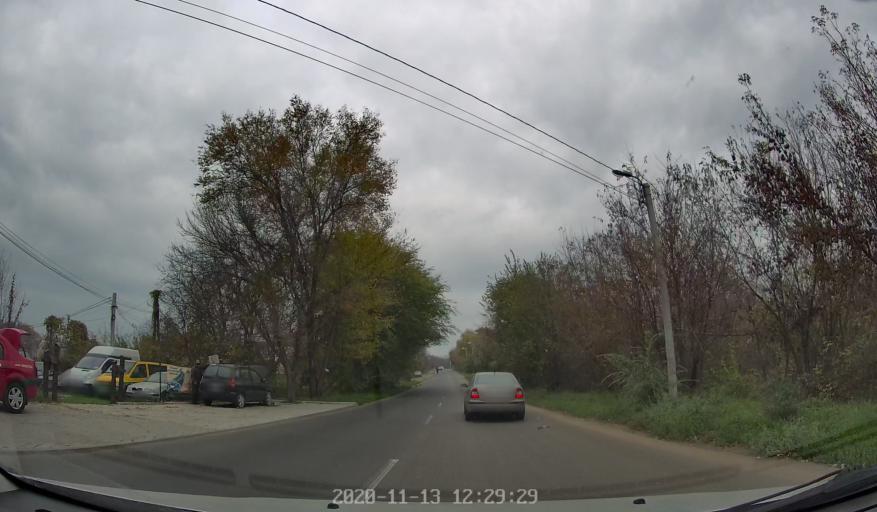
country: MD
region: Chisinau
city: Chisinau
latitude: 46.9624
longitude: 28.8346
